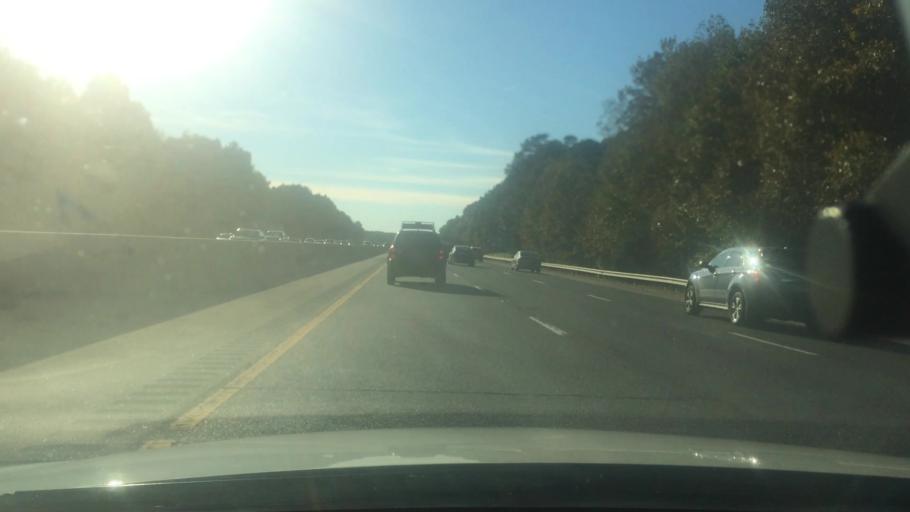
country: US
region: North Carolina
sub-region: Durham County
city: Durham
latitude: 35.9066
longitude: -78.9483
